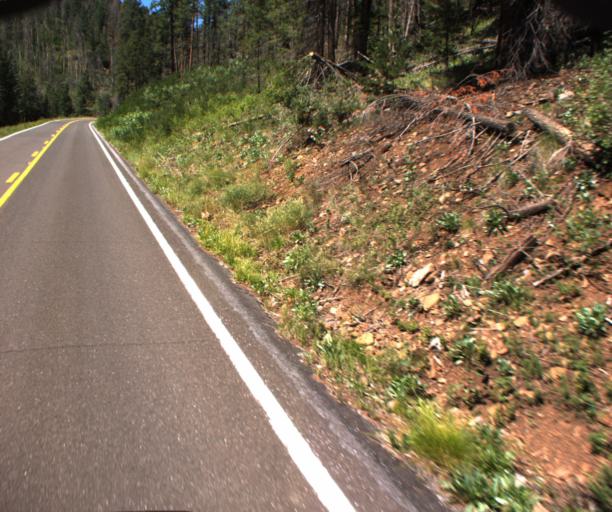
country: US
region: Arizona
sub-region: Apache County
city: Eagar
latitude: 33.6542
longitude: -109.2698
